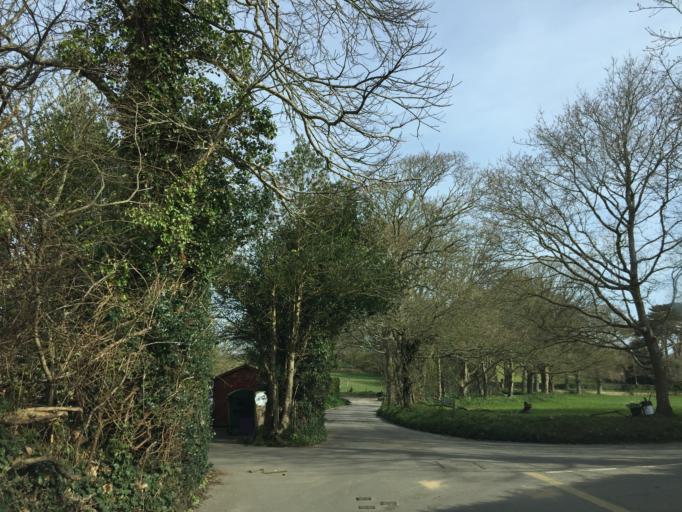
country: JE
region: St Helier
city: Saint Helier
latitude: 49.2227
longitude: -2.1395
